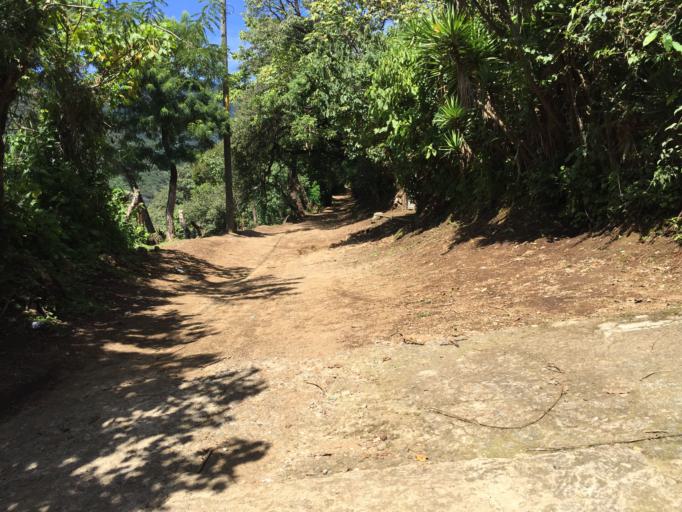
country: GT
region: Sacatepequez
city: Magdalena Milpas Altas
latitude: 14.5106
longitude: -90.6579
